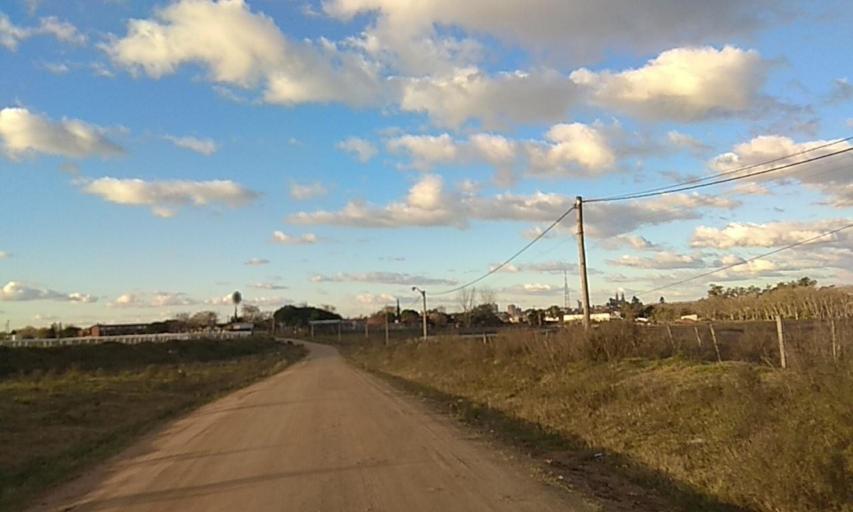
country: UY
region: Florida
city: Florida
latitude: -34.1073
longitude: -56.2322
